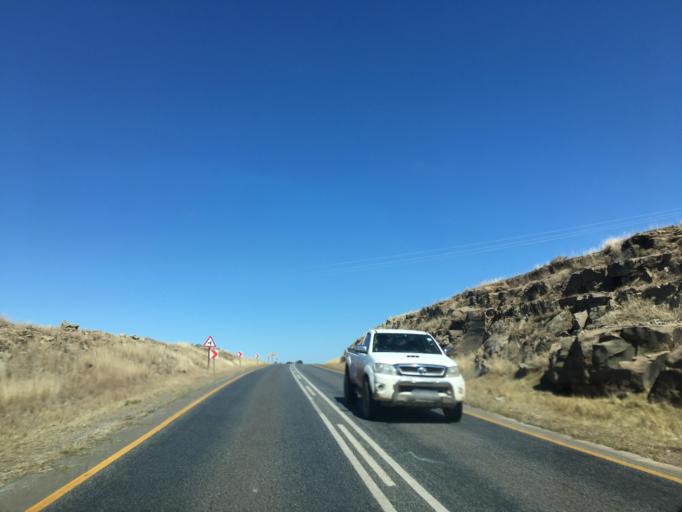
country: ZA
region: Eastern Cape
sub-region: Chris Hani District Municipality
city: Cofimvaba
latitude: -31.9106
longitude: 27.8382
